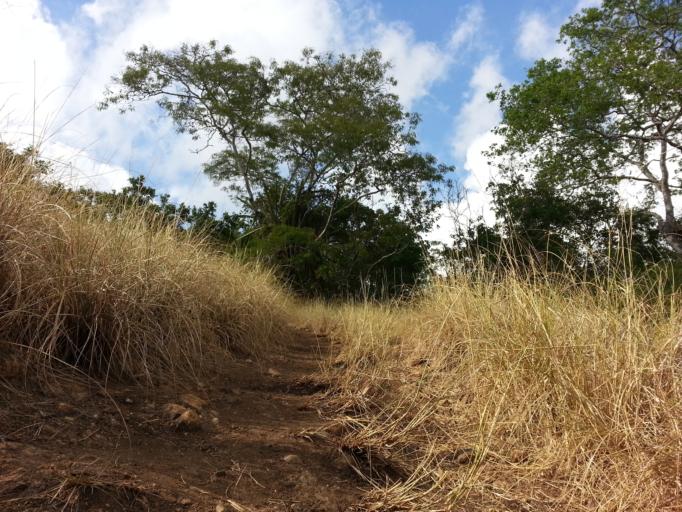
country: BR
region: Bahia
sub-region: Cruz Das Almas
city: Cruz das Almas
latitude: -12.5995
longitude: -39.1934
